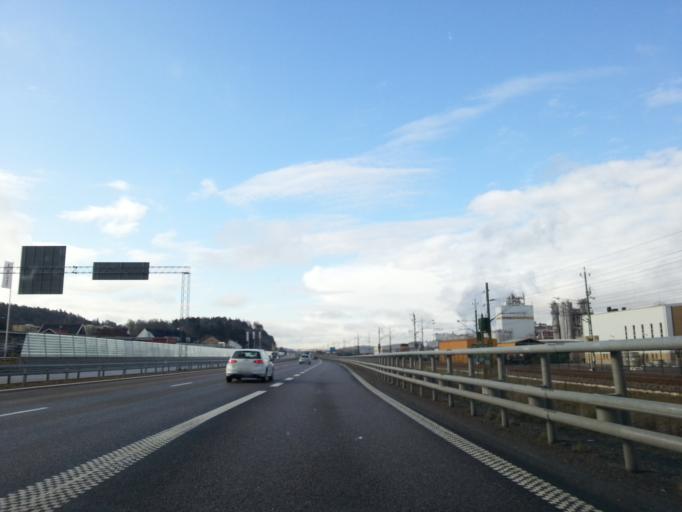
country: SE
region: Vaestra Goetaland
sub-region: Ale Kommun
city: Surte
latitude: 57.8510
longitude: 12.0138
